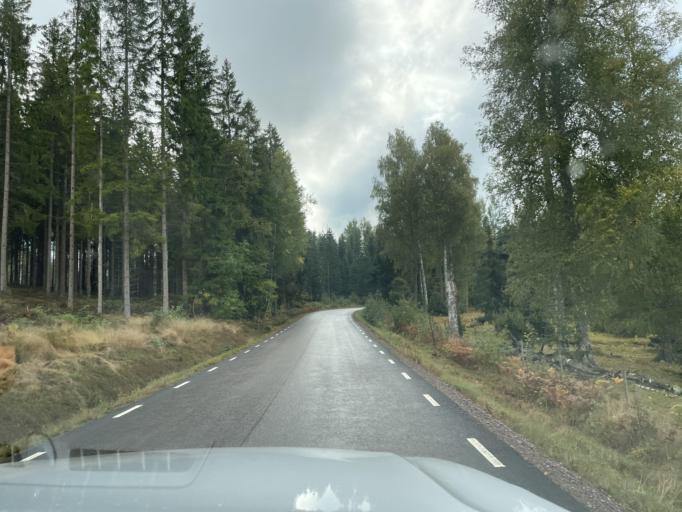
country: SE
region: Vaermland
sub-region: Karlstads Kommun
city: Skattkarr
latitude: 59.4557
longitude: 13.6106
